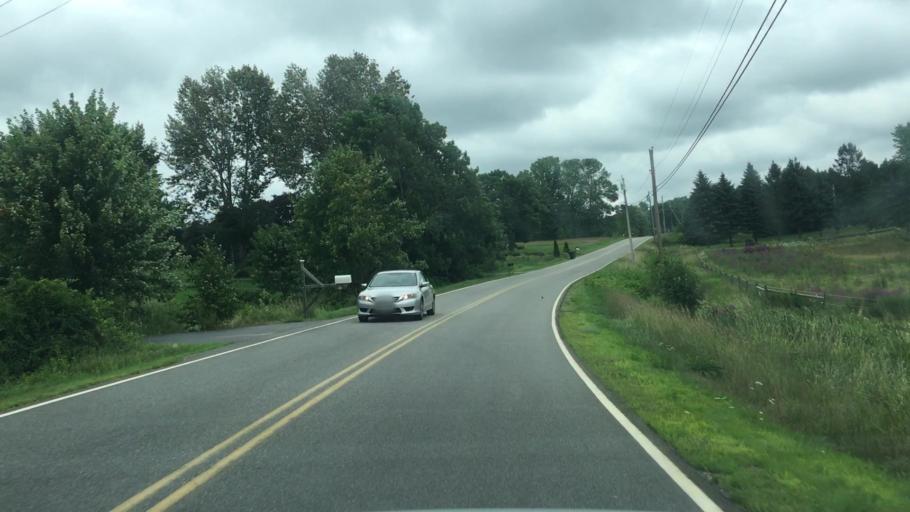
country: US
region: Maine
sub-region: York County
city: Dayton
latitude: 43.5259
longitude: -70.5208
